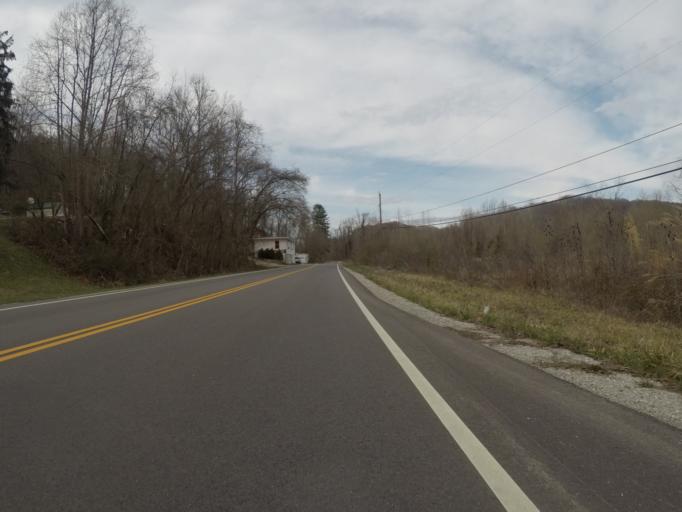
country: US
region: West Virginia
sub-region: Cabell County
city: Huntington
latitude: 38.4268
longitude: -82.4909
